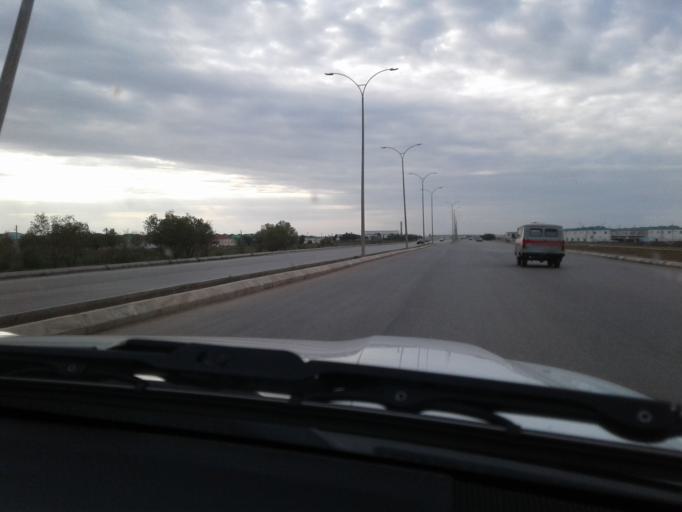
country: TM
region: Ahal
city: Tejen
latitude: 37.3680
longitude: 60.5249
